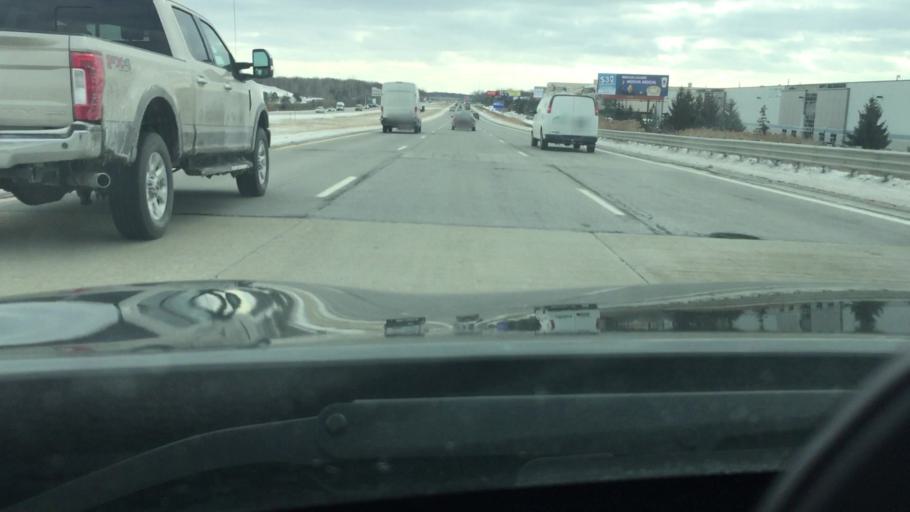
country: US
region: Michigan
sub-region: Wayne County
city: Wayne
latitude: 42.2646
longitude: -83.4410
